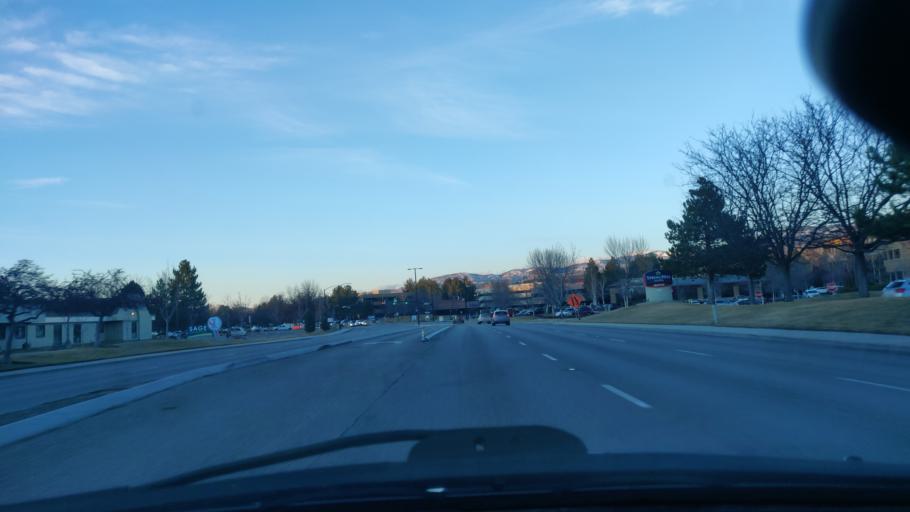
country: US
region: Idaho
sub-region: Ada County
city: Boise
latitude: 43.5949
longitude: -116.1779
